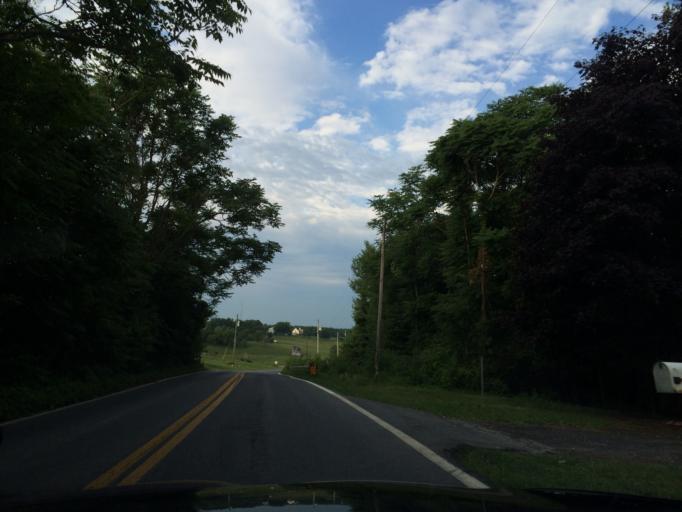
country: US
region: Maryland
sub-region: Montgomery County
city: Damascus
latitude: 39.3289
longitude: -77.2236
